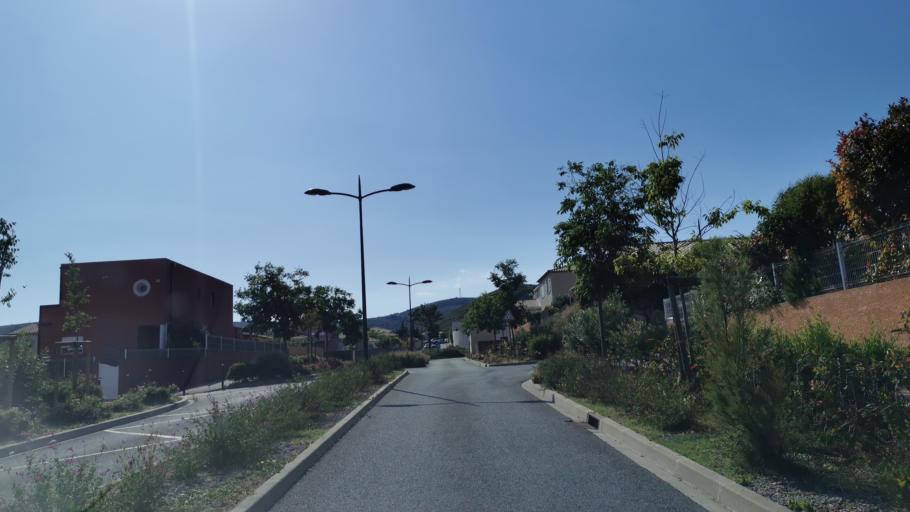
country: FR
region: Languedoc-Roussillon
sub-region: Departement de l'Aude
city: Peyriac-de-Mer
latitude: 43.1346
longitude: 2.9621
